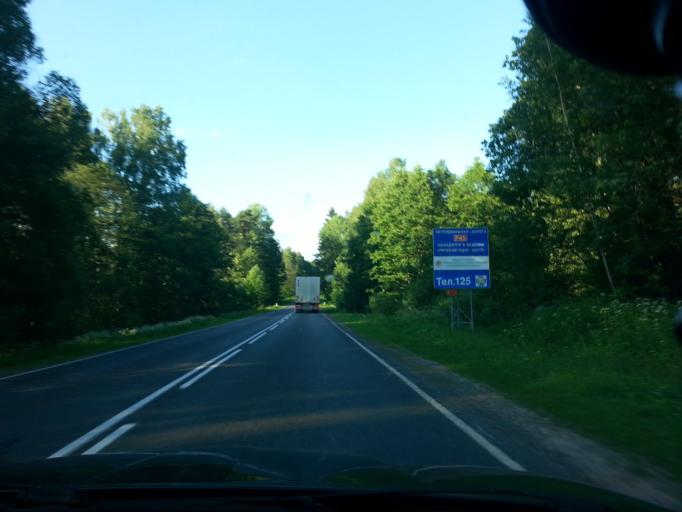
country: BY
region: Minsk
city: Svir
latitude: 54.8702
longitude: 26.3480
